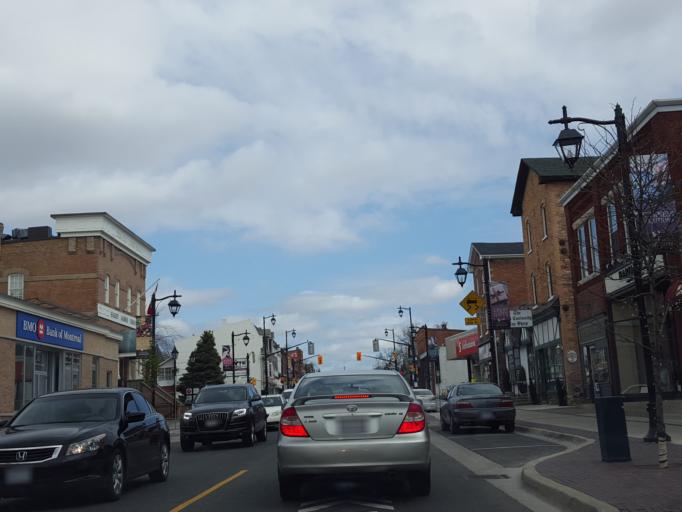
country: CA
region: Ontario
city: Markham
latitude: 43.8769
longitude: -79.2606
